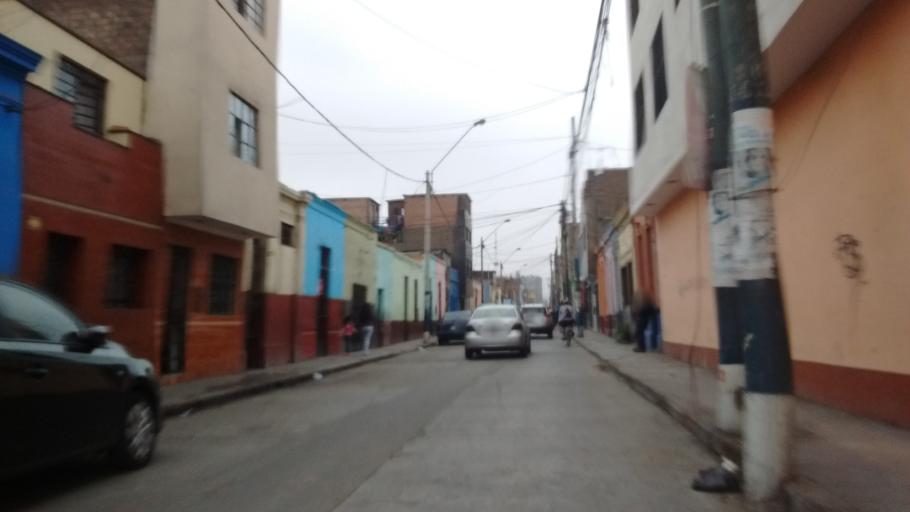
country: PE
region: Lima
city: Lima
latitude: -12.0683
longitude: -77.0278
